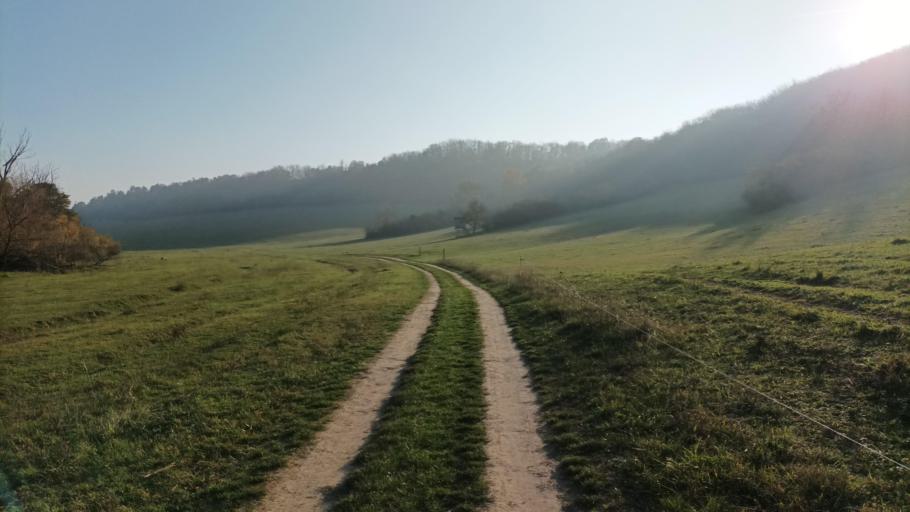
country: HU
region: Tolna
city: Szentgalpuszta
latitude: 46.3291
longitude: 18.6070
